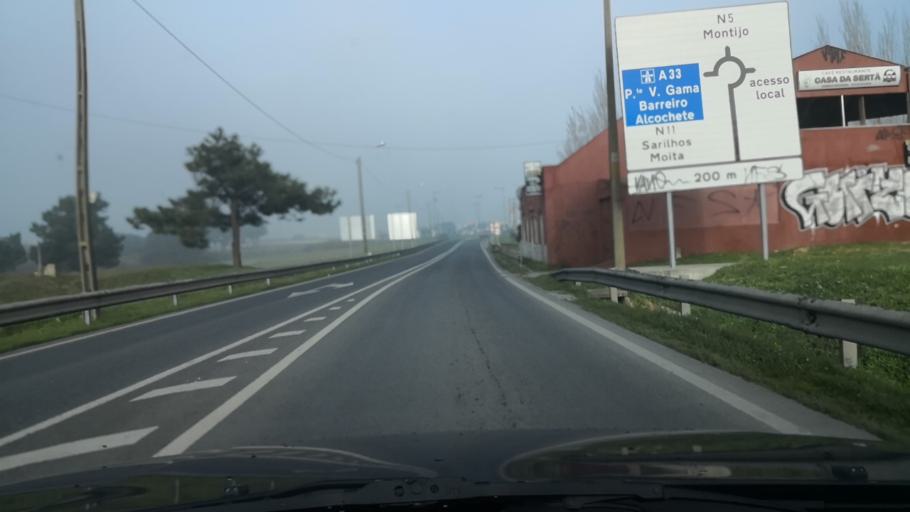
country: PT
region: Setubal
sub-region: Montijo
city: Montijo
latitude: 38.6846
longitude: -8.9426
